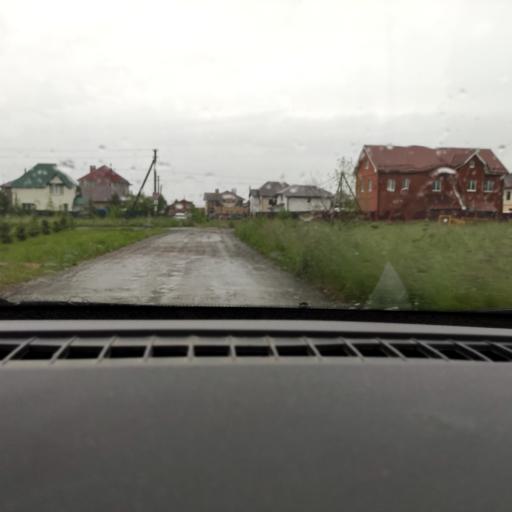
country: RU
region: Perm
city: Perm
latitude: 58.0432
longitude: 56.3738
